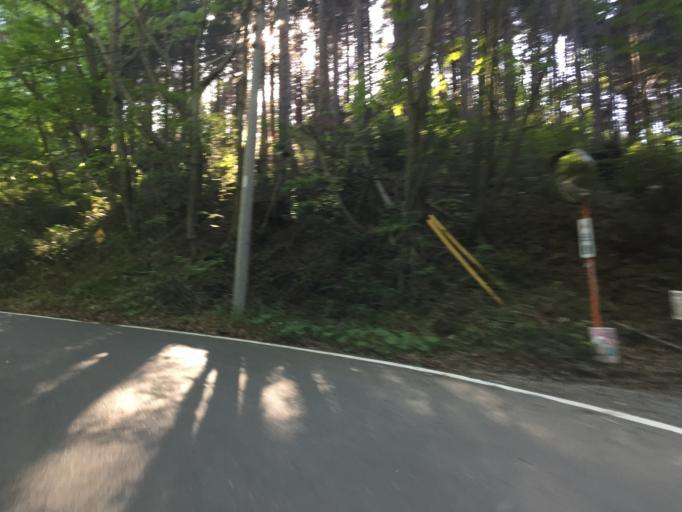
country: JP
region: Ibaraki
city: Kitaibaraki
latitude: 36.9007
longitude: 140.6186
